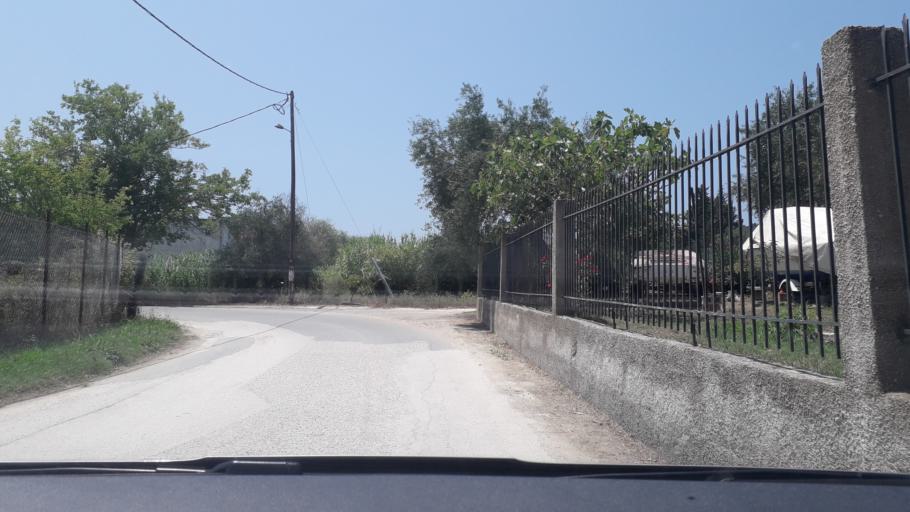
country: GR
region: Ionian Islands
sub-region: Nomos Kerkyras
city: Lefkimmi
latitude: 39.3795
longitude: 20.1151
